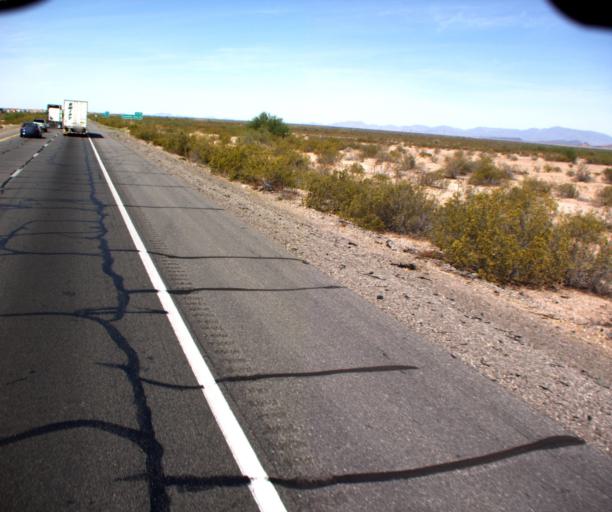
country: US
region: Arizona
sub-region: La Paz County
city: Salome
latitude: 33.5341
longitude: -113.1381
